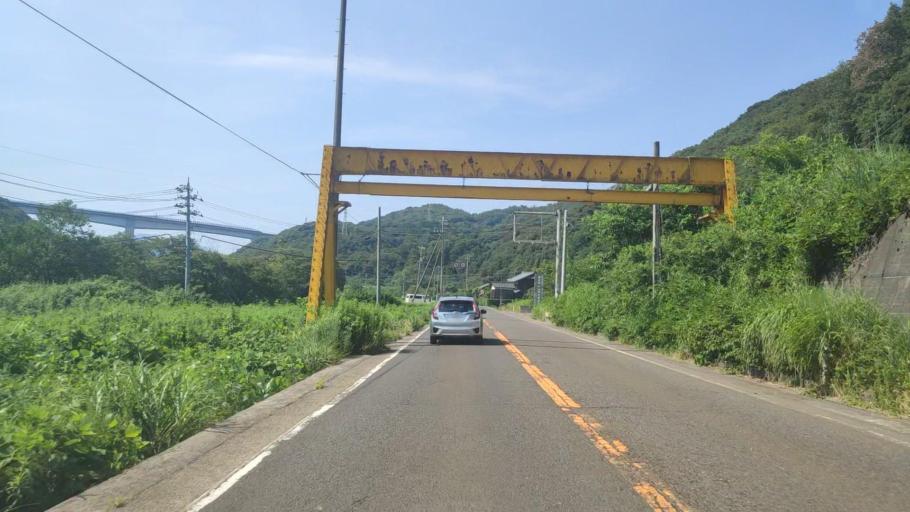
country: JP
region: Fukui
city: Tsuruga
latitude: 35.6180
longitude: 136.0829
